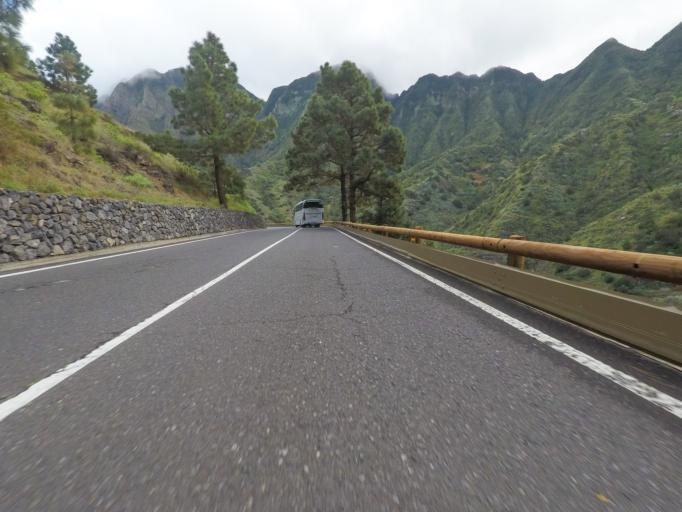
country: ES
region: Canary Islands
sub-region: Provincia de Santa Cruz de Tenerife
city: Hermigua
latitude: 28.1405
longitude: -17.1986
